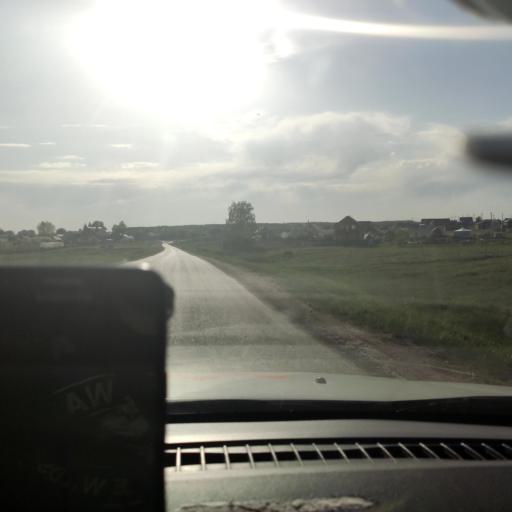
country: RU
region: Bashkortostan
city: Avdon
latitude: 54.5119
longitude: 55.8195
